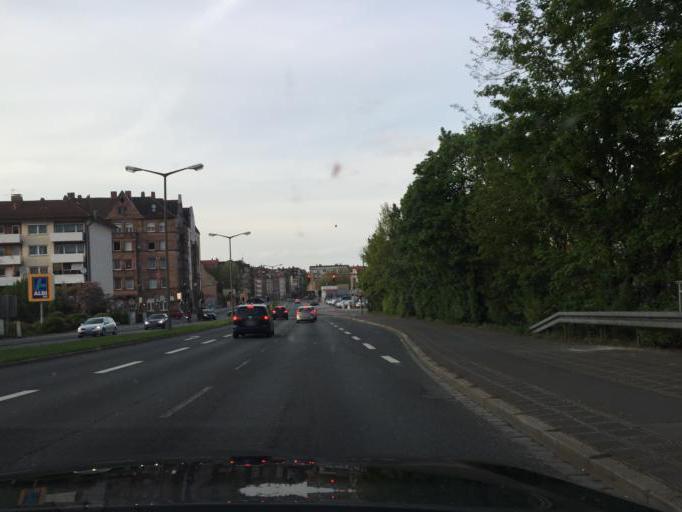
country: DE
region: Bavaria
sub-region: Regierungsbezirk Mittelfranken
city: Wetzendorf
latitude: 49.4535
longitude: 11.0396
